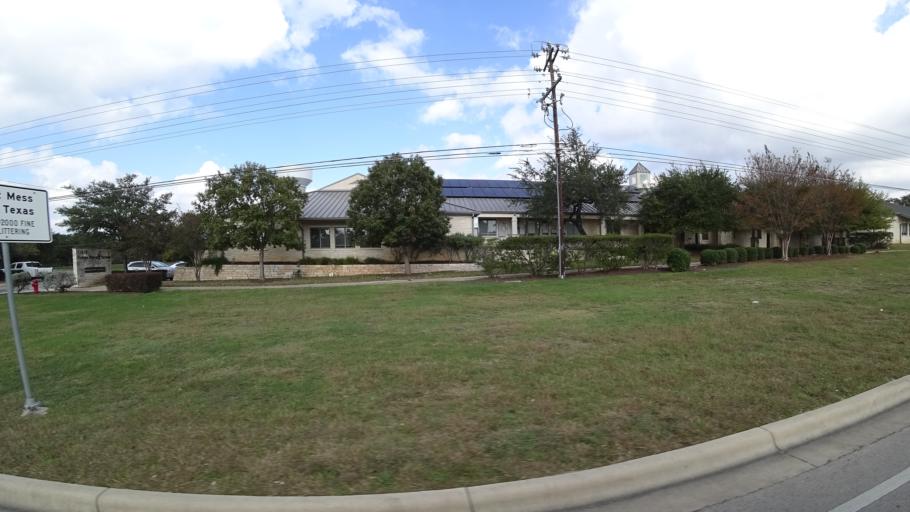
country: US
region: Texas
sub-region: Williamson County
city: Anderson Mill
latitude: 30.4560
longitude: -97.8282
